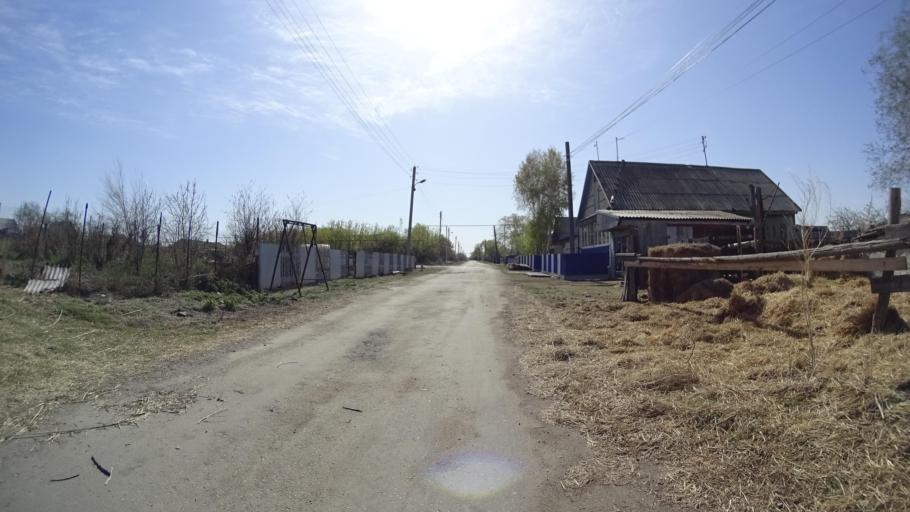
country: RU
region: Chelyabinsk
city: Chesma
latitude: 53.7946
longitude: 61.0305
